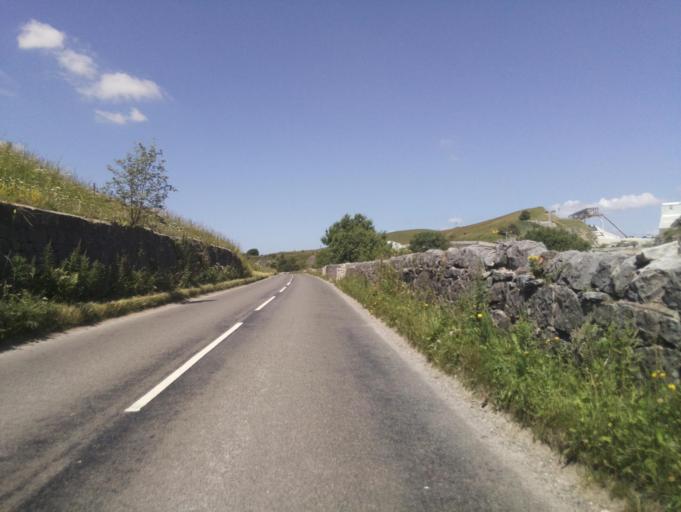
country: GB
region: England
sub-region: Derbyshire
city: Buxton
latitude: 53.2904
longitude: -1.8660
